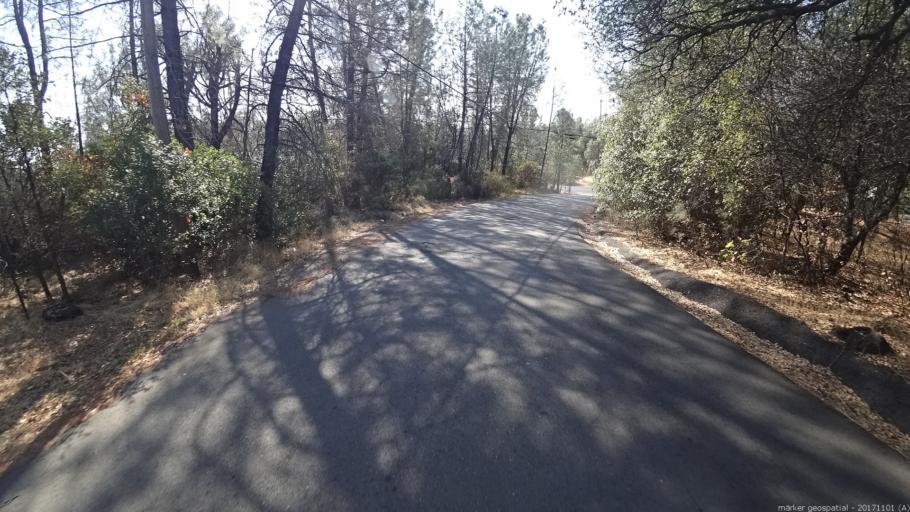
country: US
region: California
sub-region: Shasta County
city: Central Valley (historical)
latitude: 40.6826
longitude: -122.3754
